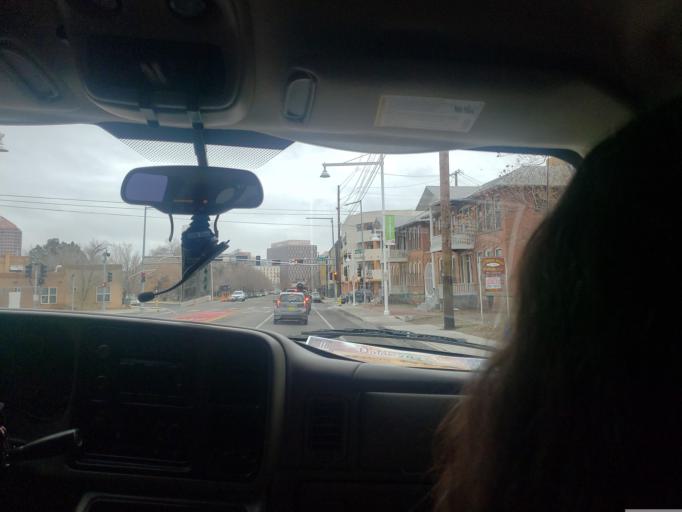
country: US
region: New Mexico
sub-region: Bernalillo County
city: Albuquerque
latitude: 35.0868
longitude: -106.6589
